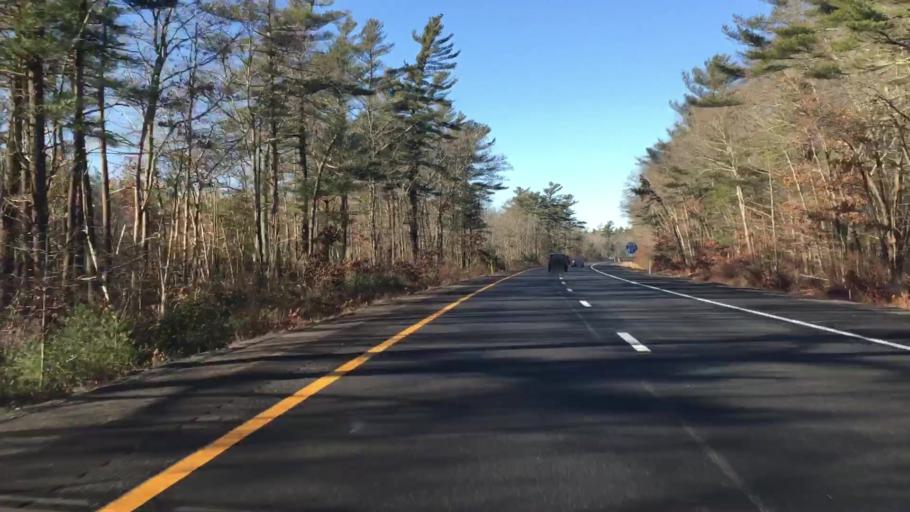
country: US
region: Massachusetts
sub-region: Plymouth County
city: West Wareham
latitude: 41.8141
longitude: -70.7941
